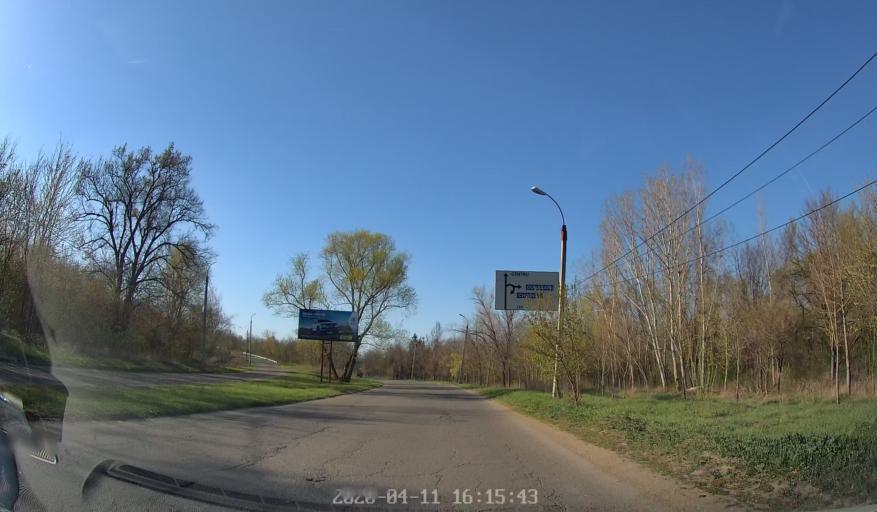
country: MD
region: Chisinau
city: Vadul lui Voda
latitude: 47.0813
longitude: 29.0919
